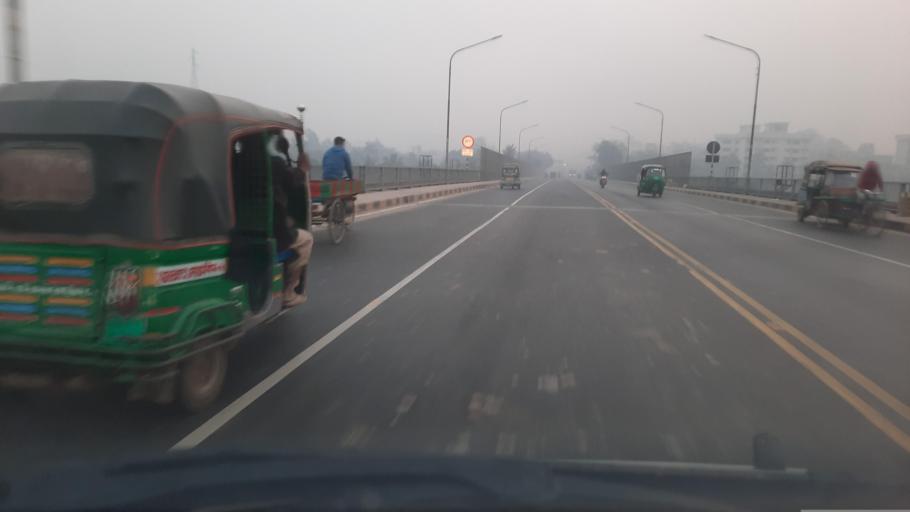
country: BD
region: Dhaka
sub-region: Dhaka
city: Dhaka
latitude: 23.6873
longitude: 90.4271
